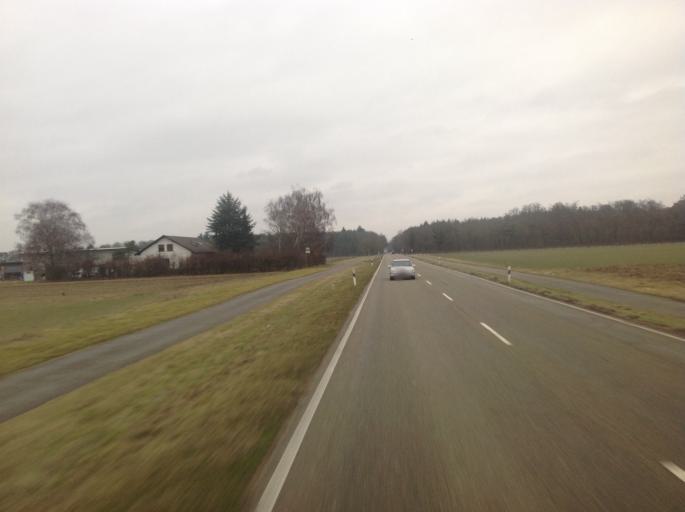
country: DE
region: Baden-Wuerttemberg
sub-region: Karlsruhe Region
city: Hugelsheim
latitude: 48.8027
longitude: 8.1244
